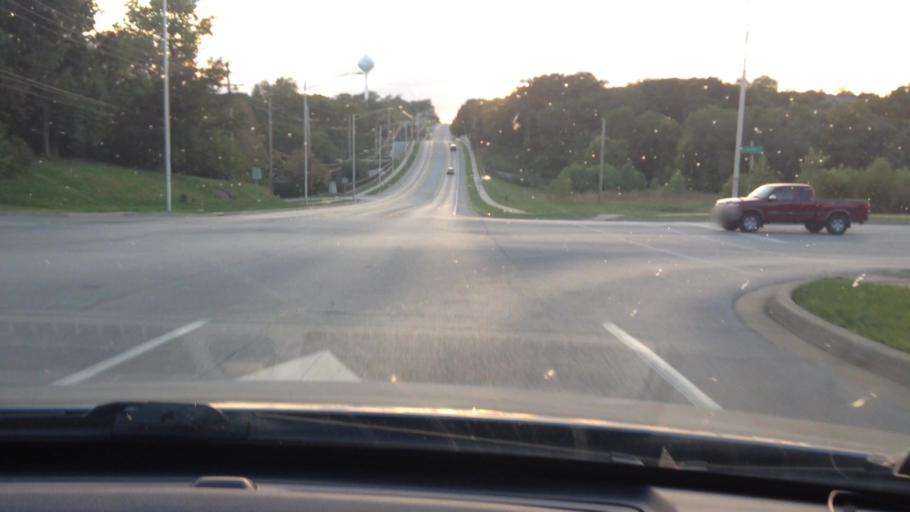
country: US
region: Missouri
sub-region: Platte County
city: Weatherby Lake
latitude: 39.2471
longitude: -94.6859
